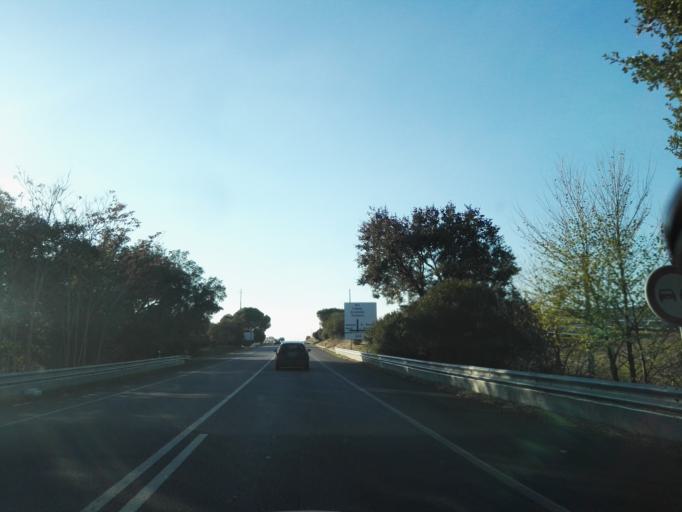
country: PT
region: Evora
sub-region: Estremoz
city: Estremoz
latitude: 38.8359
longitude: -7.6542
